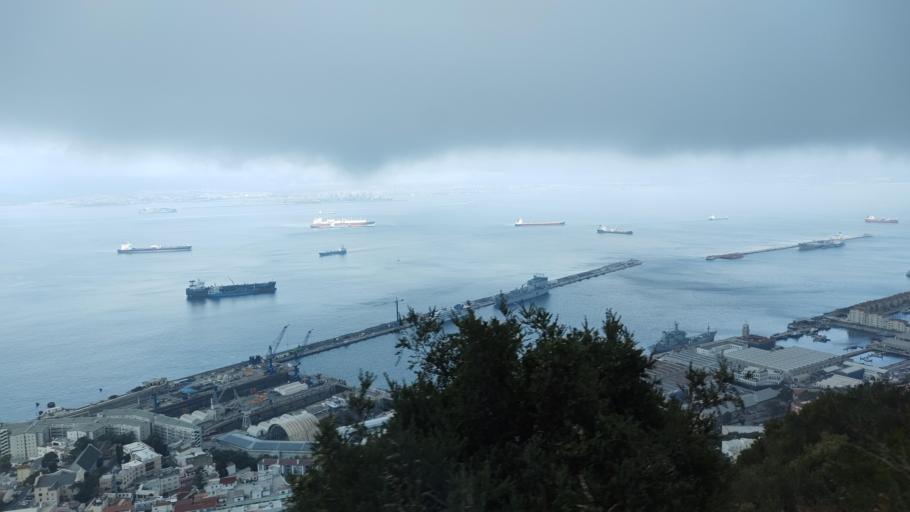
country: GI
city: Gibraltar
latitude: 36.1266
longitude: -5.3467
